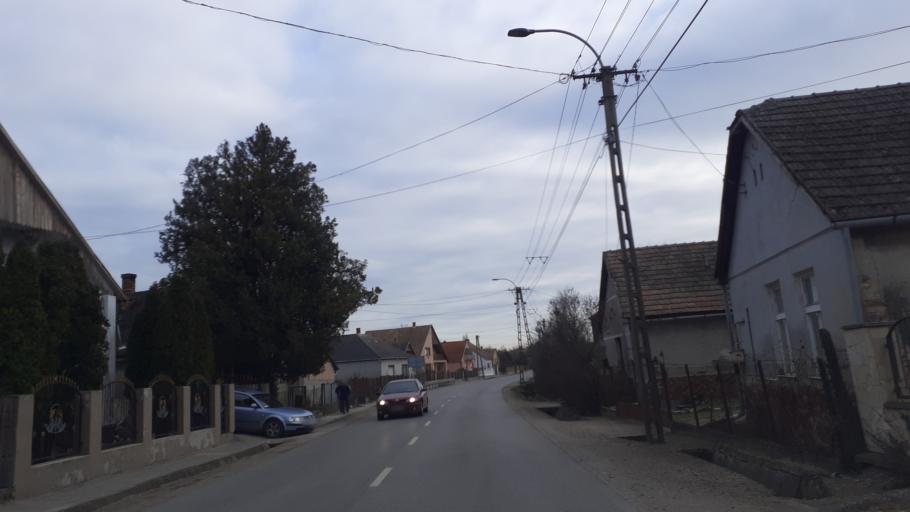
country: HU
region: Fejer
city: Sarkeresztur
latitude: 47.0063
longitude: 18.5484
